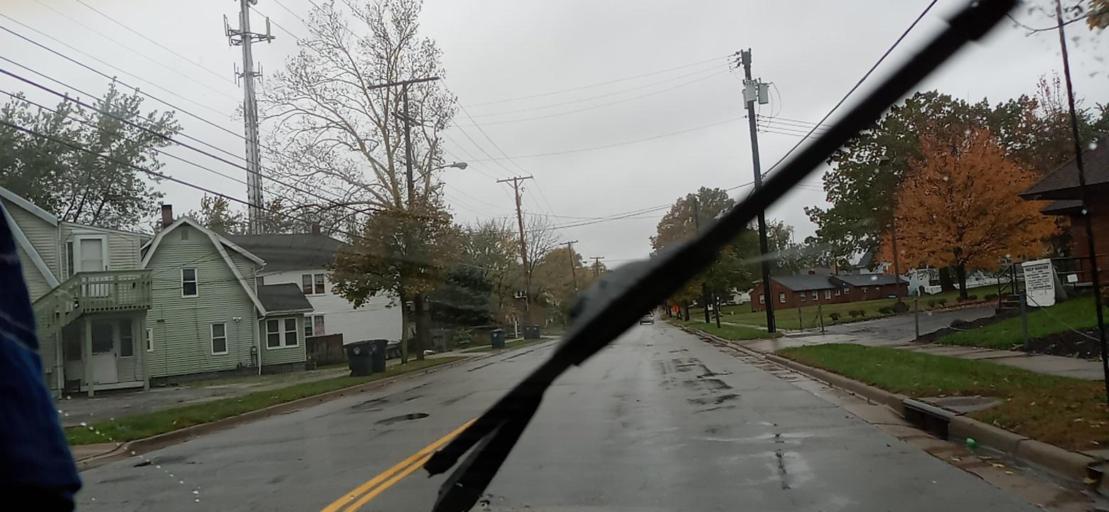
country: US
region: Ohio
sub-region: Summit County
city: Akron
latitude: 41.0634
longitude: -81.5546
